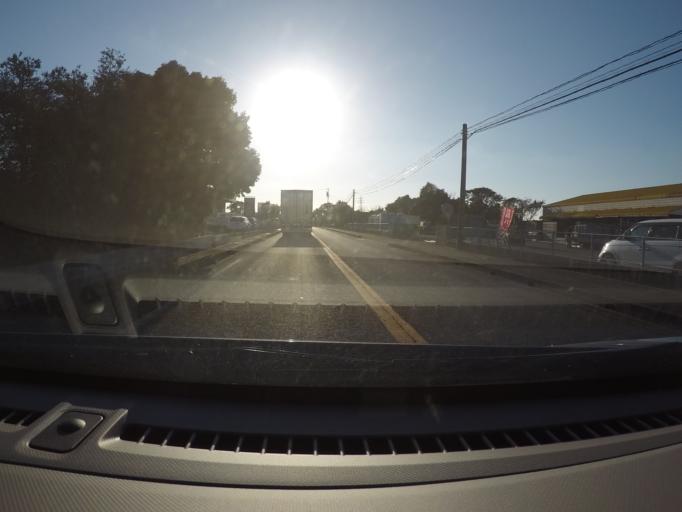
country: JP
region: Kagoshima
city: Izumi
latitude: 32.0966
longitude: 130.3014
